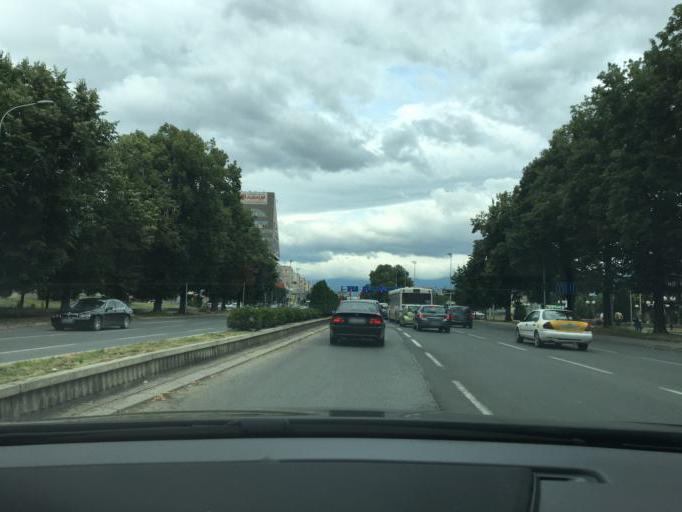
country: MK
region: Karpos
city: Skopje
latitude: 41.9974
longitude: 21.4407
